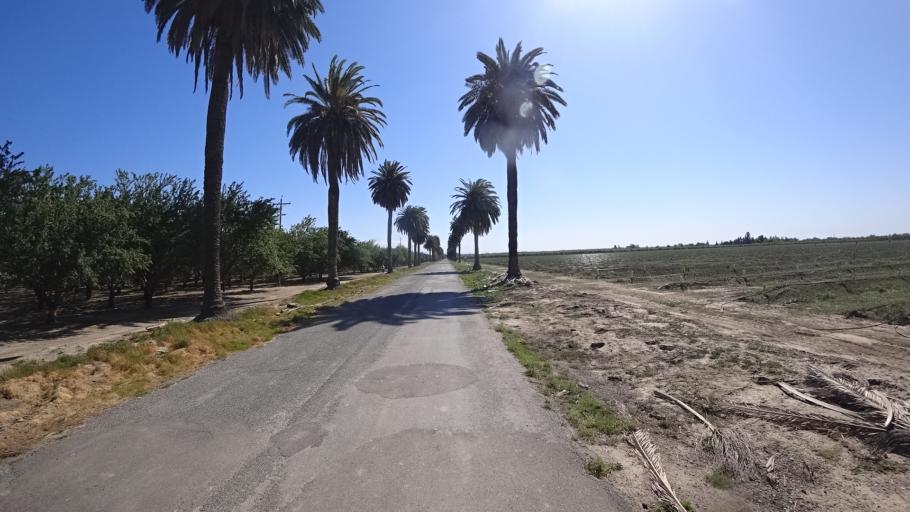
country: US
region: California
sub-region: Glenn County
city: Hamilton City
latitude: 39.7374
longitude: -122.0261
